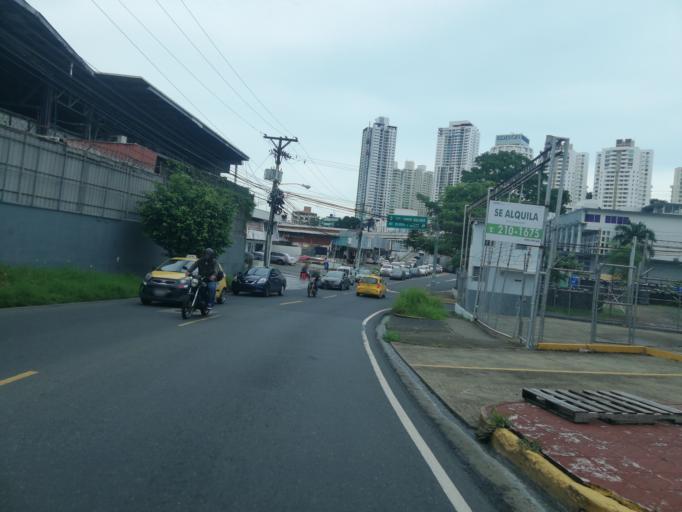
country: PA
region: Panama
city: Panama
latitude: 8.9964
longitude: -79.5357
